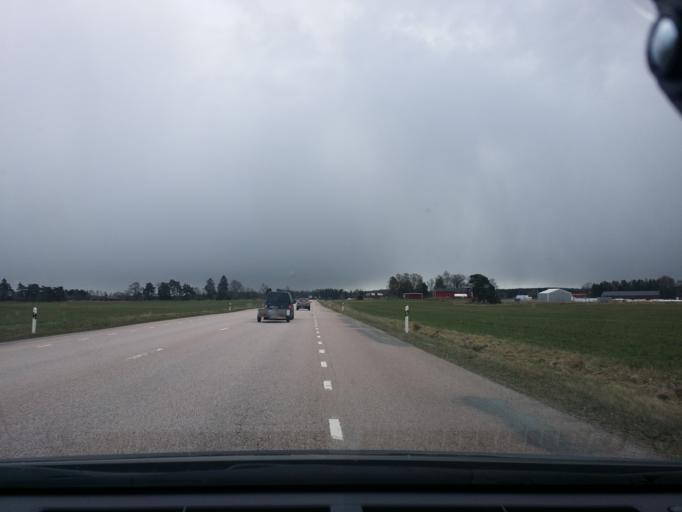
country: SE
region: Uppsala
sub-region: Enkopings Kommun
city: Enkoping
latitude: 59.6893
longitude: 17.0327
